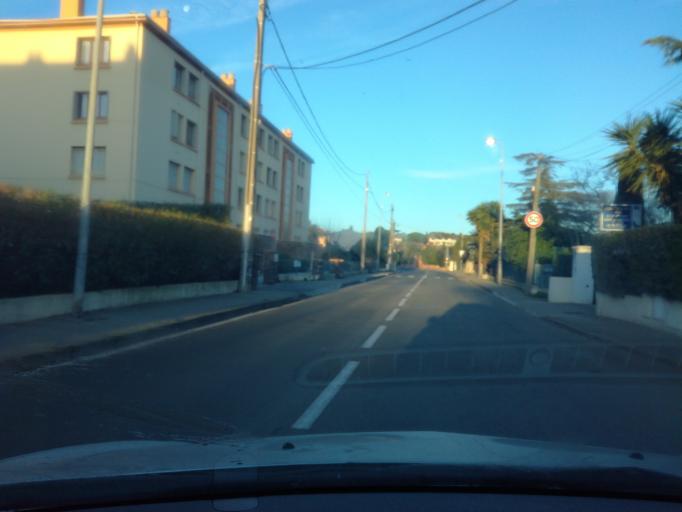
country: FR
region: Provence-Alpes-Cote d'Azur
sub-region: Departement du Var
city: Frejus
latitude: 43.4317
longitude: 6.7450
